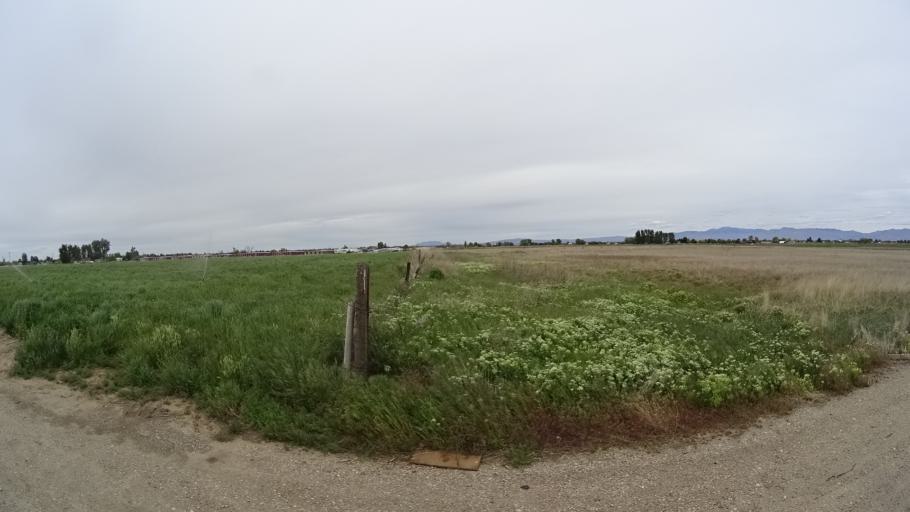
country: US
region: Idaho
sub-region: Ada County
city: Kuna
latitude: 43.4879
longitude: -116.3895
